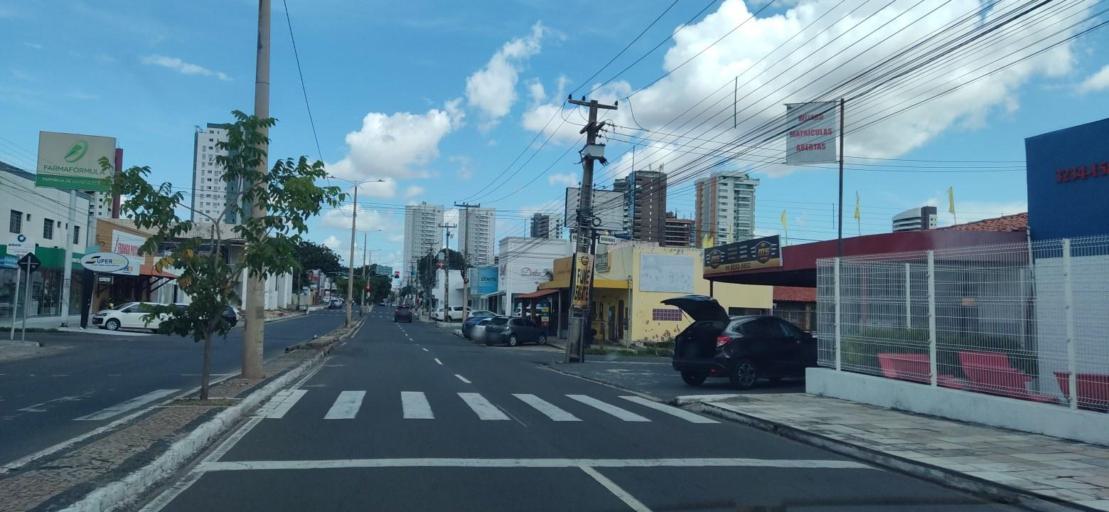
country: BR
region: Piaui
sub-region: Teresina
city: Teresina
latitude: -5.0719
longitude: -42.7920
